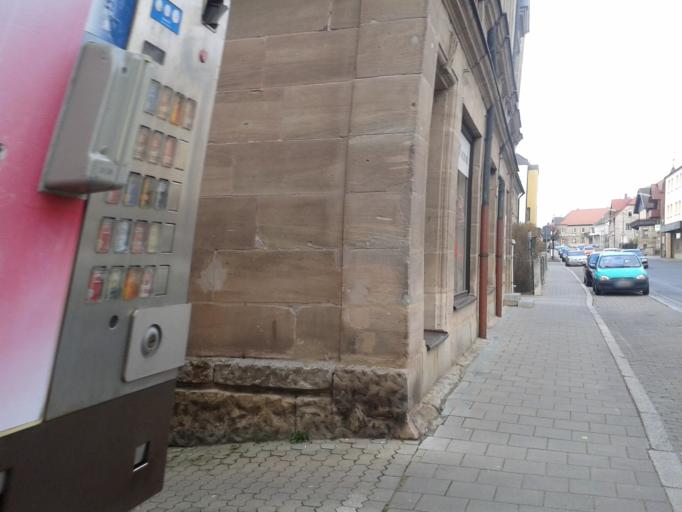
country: DE
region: Bavaria
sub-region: Regierungsbezirk Mittelfranken
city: Cadolzburg
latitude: 49.4577
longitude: 10.8536
